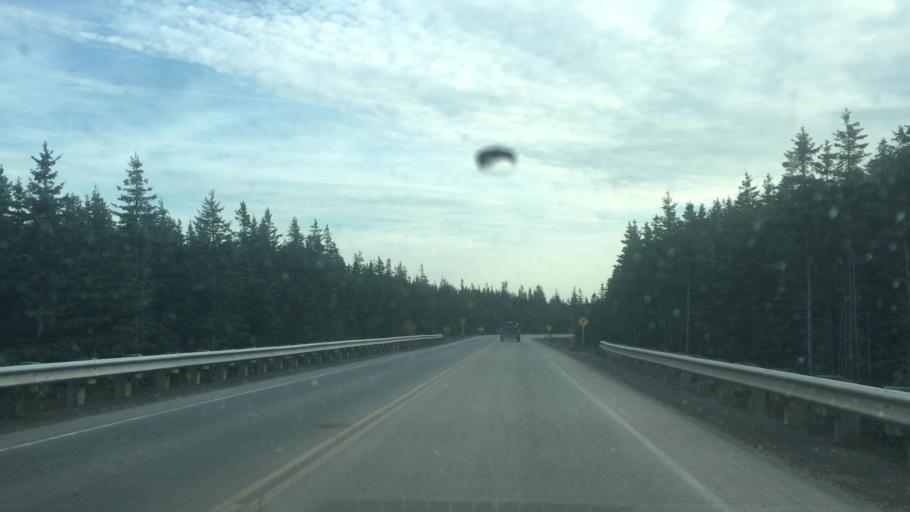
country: CA
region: Nova Scotia
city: Sydney Mines
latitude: 46.8011
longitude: -60.8441
